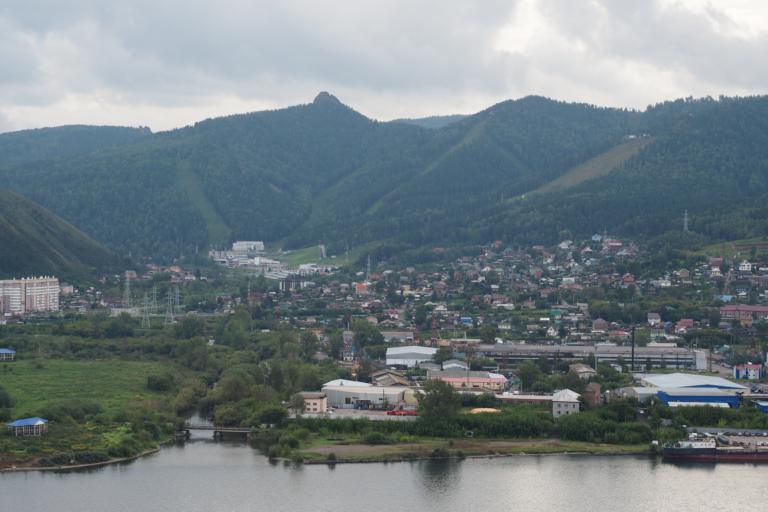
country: RU
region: Krasnoyarskiy
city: Krasnoyarsk
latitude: 55.9863
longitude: 92.7782
